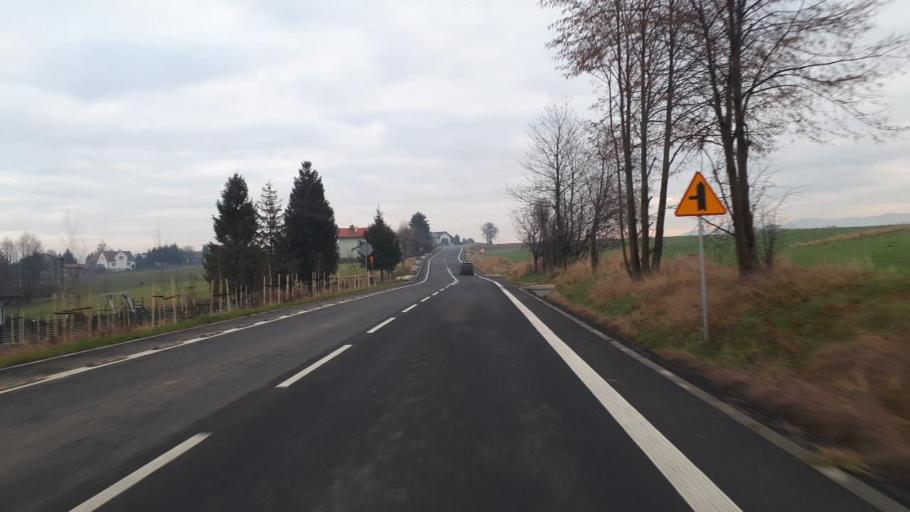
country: PL
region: Silesian Voivodeship
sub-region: Powiat bielski
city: Mazancowice
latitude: 49.8546
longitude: 18.9583
